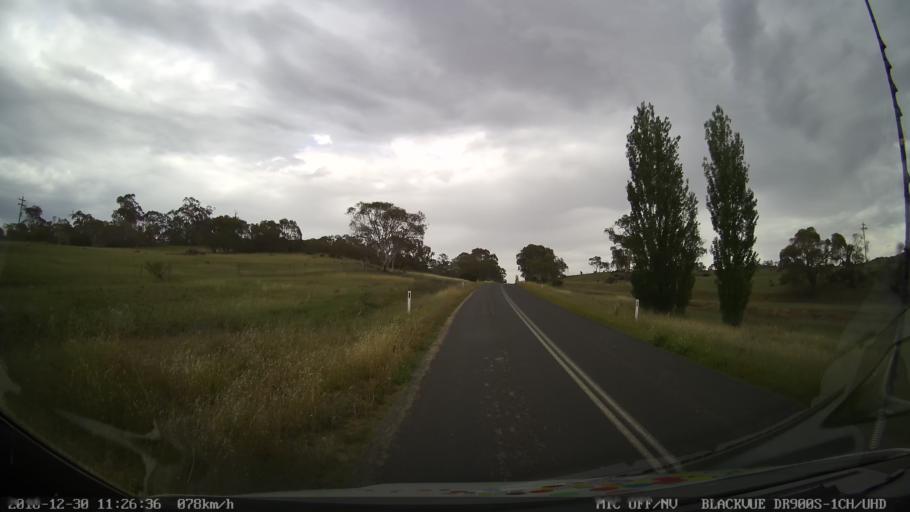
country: AU
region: New South Wales
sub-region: Snowy River
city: Jindabyne
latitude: -36.4671
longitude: 148.6323
